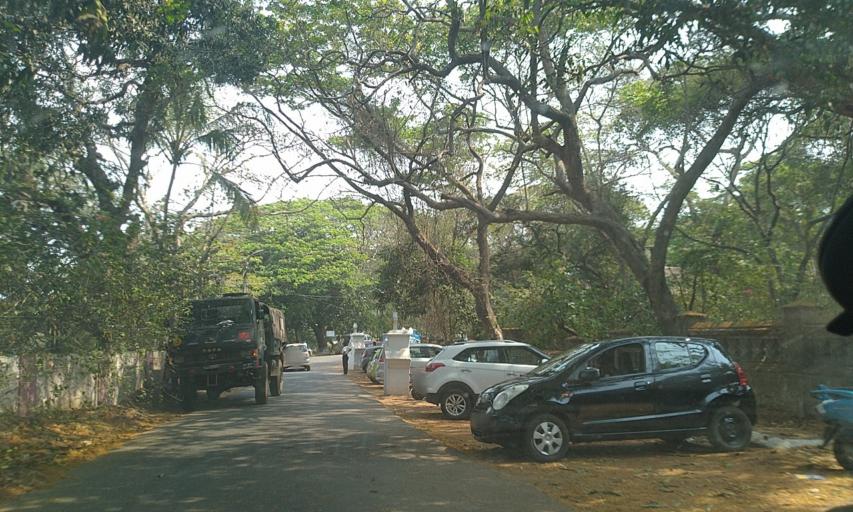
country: IN
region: Goa
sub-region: North Goa
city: Panaji
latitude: 15.4933
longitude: 73.8268
